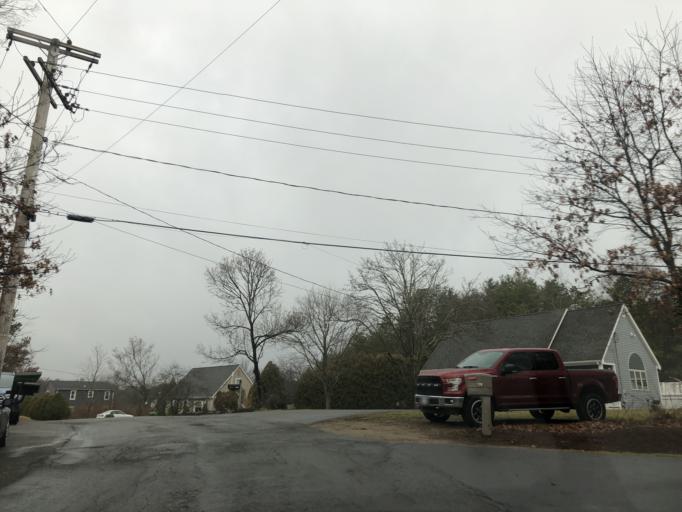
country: US
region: Massachusetts
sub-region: Norfolk County
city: Plainville
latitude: 42.0076
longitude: -71.2782
